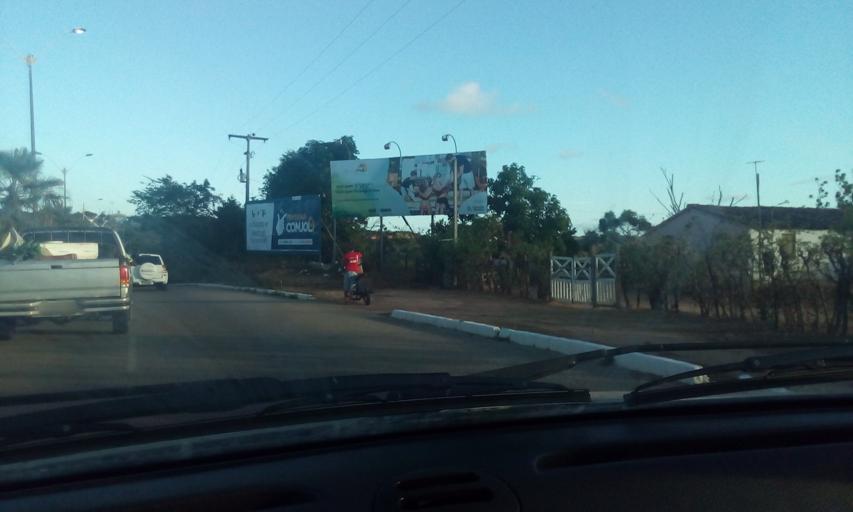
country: BR
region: Rio Grande do Norte
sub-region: Parnamirim
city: Parnamirim
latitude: -5.9662
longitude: -35.1434
